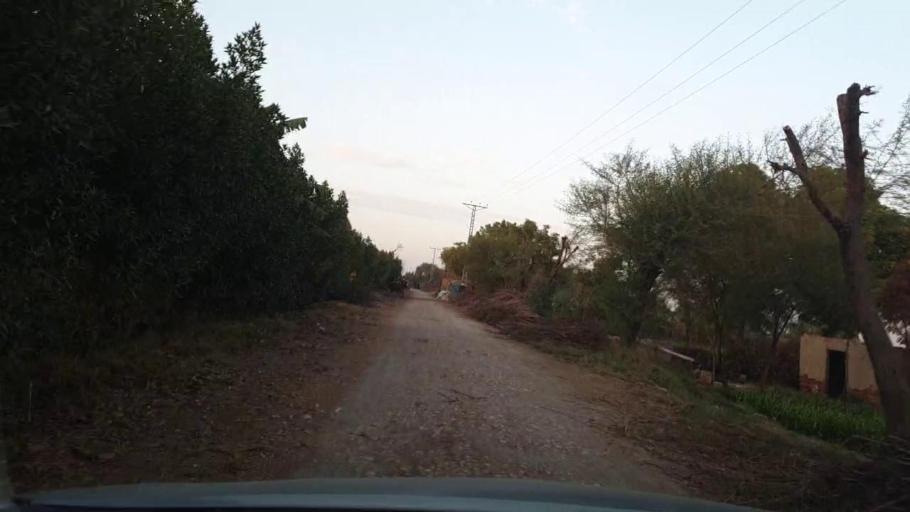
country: PK
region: Sindh
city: Matiari
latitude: 25.6065
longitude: 68.4814
